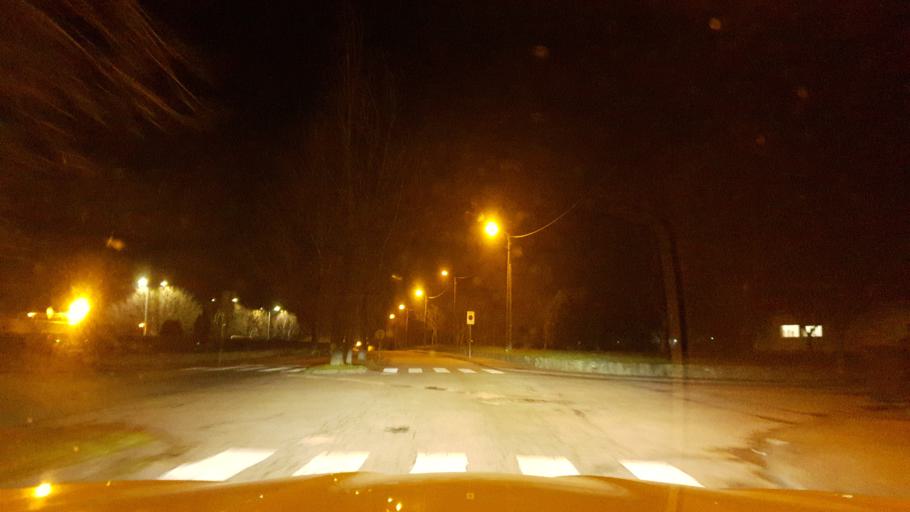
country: PT
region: Porto
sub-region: Maia
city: Leca do Bailio
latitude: 41.2068
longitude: -8.6368
